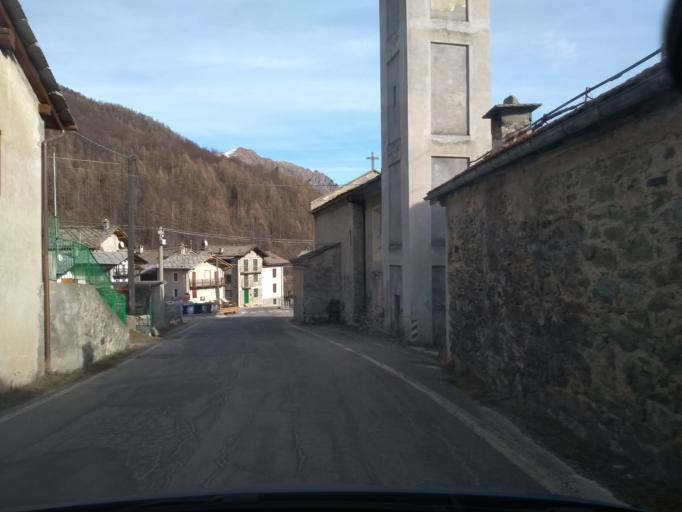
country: IT
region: Piedmont
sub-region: Provincia di Torino
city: Balme
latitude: 45.3117
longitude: 7.2582
